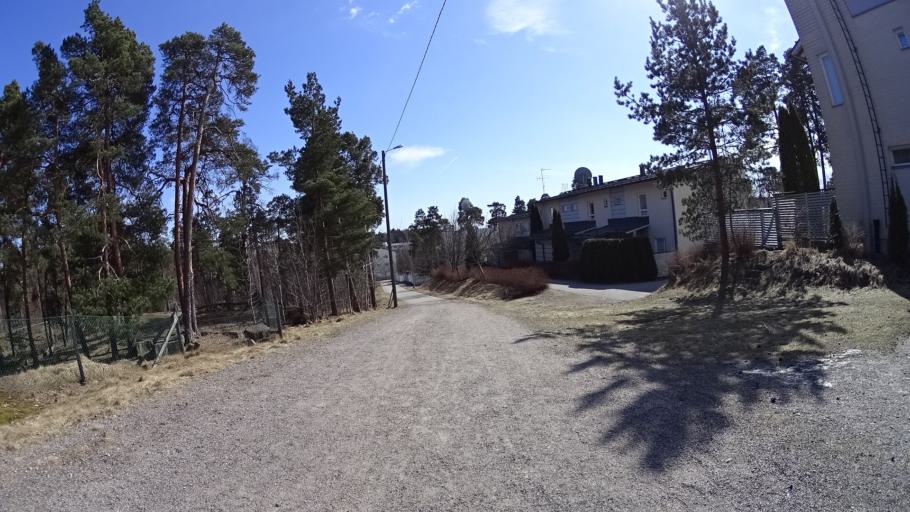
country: FI
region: Uusimaa
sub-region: Helsinki
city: Kilo
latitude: 60.2205
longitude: 24.7815
